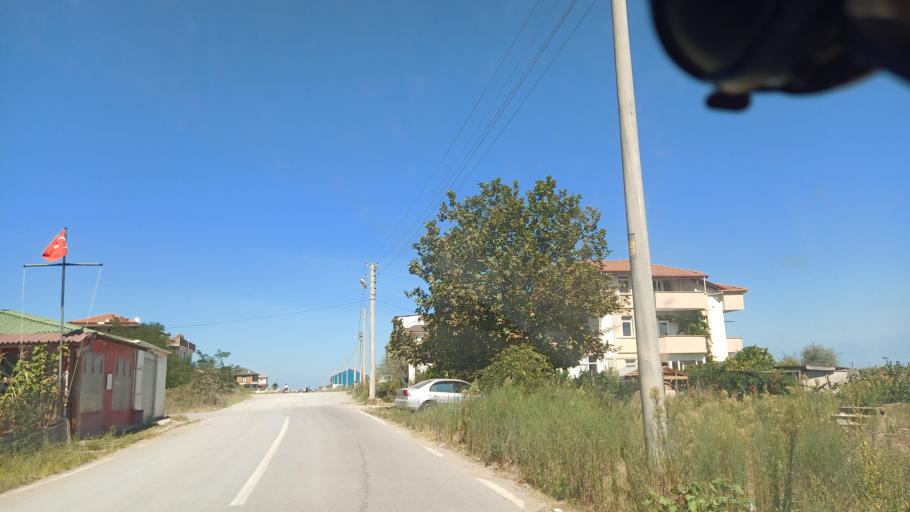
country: TR
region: Sakarya
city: Karasu
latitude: 41.1209
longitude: 30.6551
